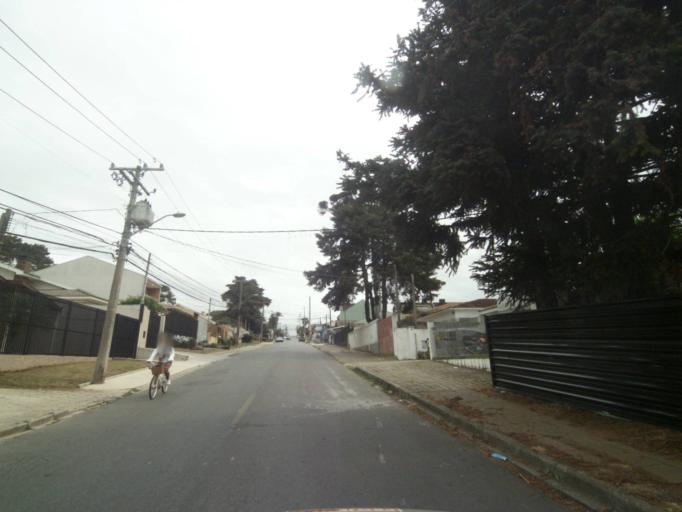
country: BR
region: Parana
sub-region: Pinhais
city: Pinhais
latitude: -25.4830
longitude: -49.2244
